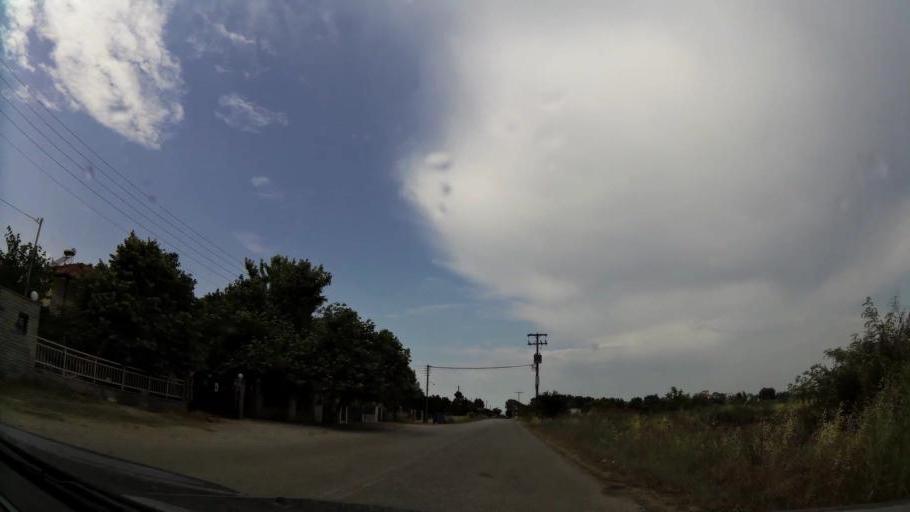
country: GR
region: Central Macedonia
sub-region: Nomos Pierias
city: Korinos
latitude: 40.2959
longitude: 22.6100
